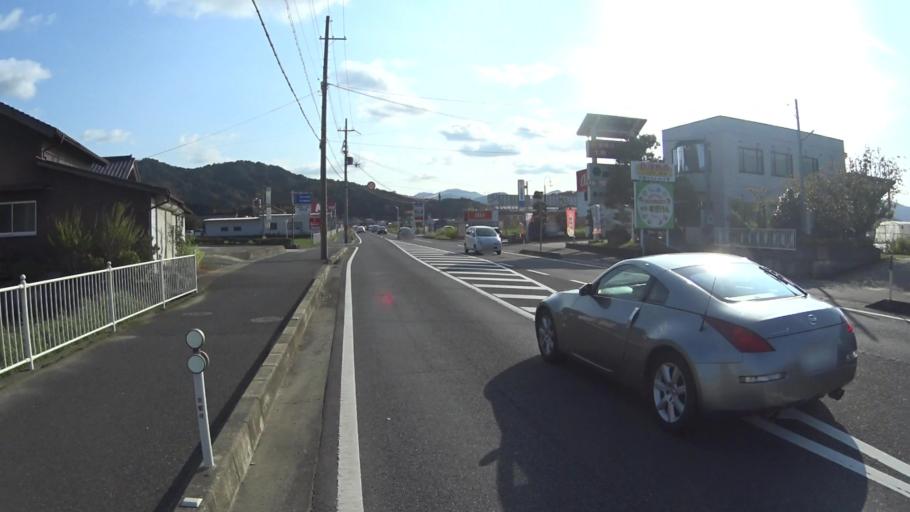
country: JP
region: Kyoto
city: Miyazu
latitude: 35.5313
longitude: 135.1217
